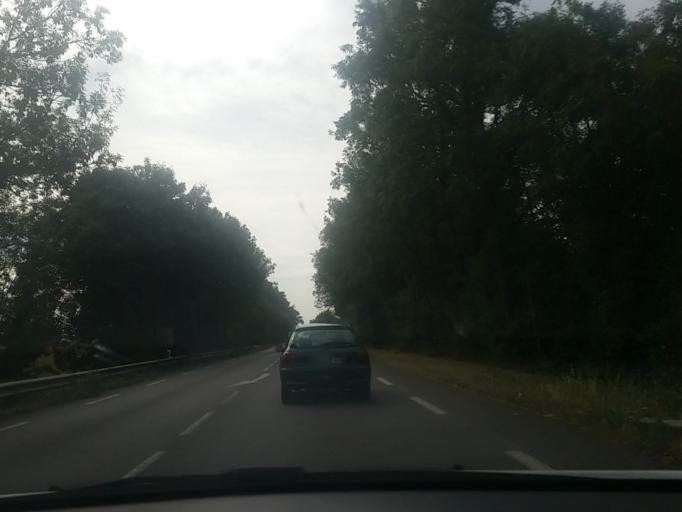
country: FR
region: Pays de la Loire
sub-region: Departement de la Vendee
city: Sainte-Cecile
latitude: 46.7755
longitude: -1.1136
